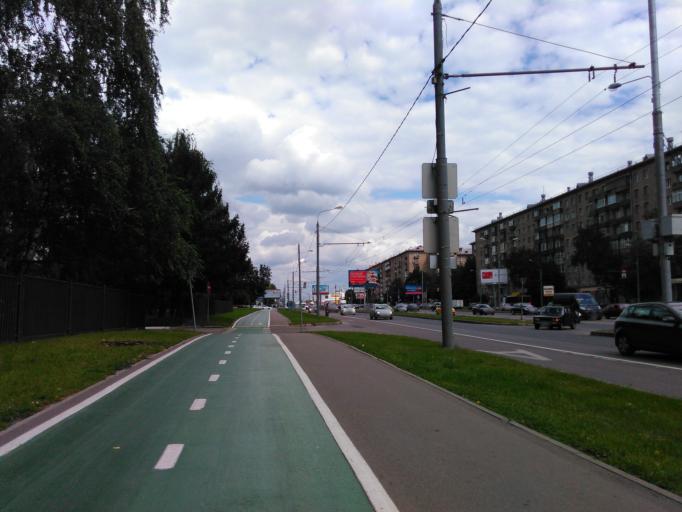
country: RU
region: Moskovskaya
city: Semenovskoye
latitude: 55.6885
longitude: 37.5267
